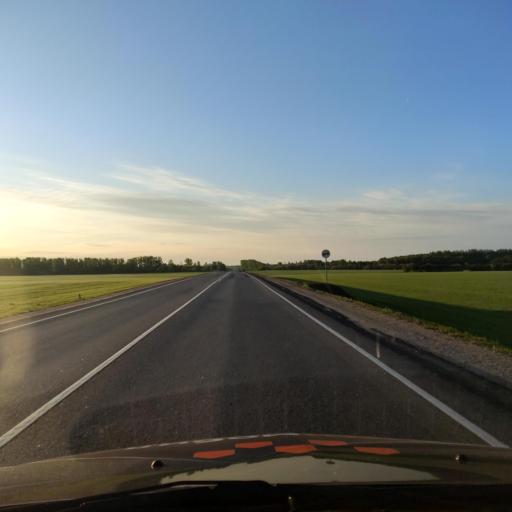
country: RU
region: Orjol
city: Livny
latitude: 52.4468
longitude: 37.5216
